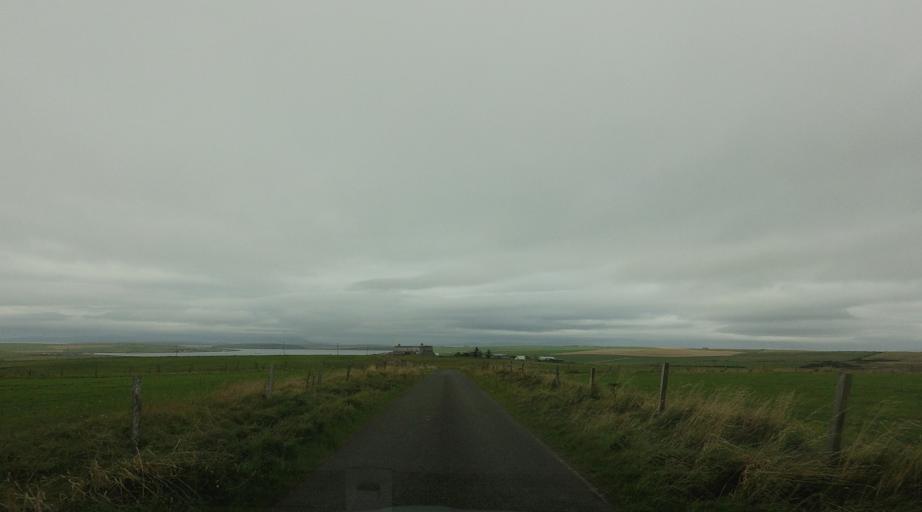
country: GB
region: Scotland
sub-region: Orkney Islands
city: Orkney
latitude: 58.8011
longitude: -2.9541
